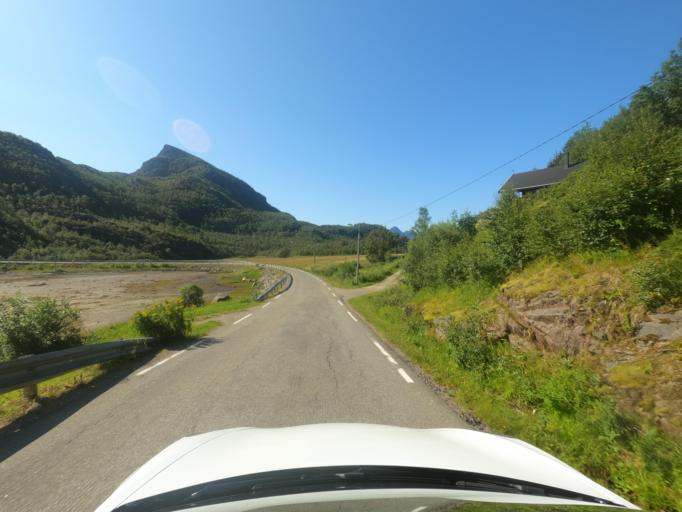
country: NO
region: Nordland
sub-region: Hadsel
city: Stokmarknes
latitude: 68.3007
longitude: 15.0395
